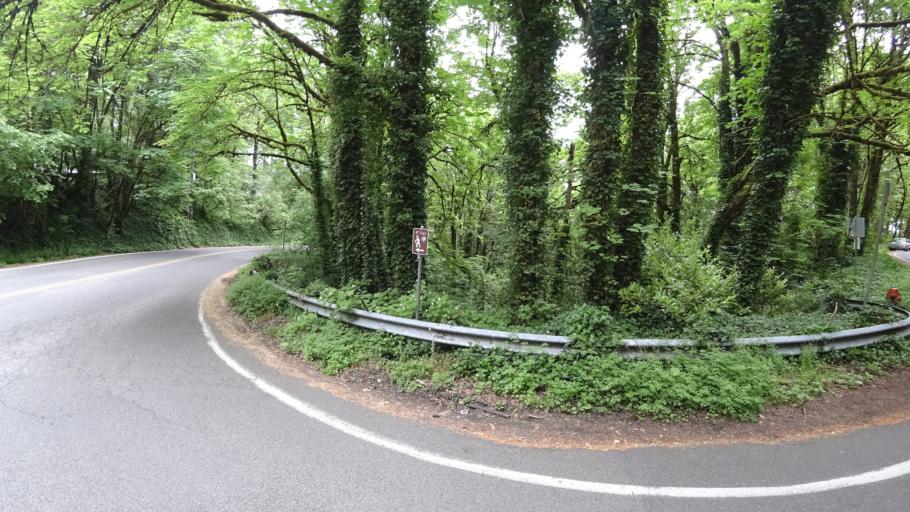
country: US
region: Oregon
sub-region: Multnomah County
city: Portland
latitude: 45.4951
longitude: -122.6978
